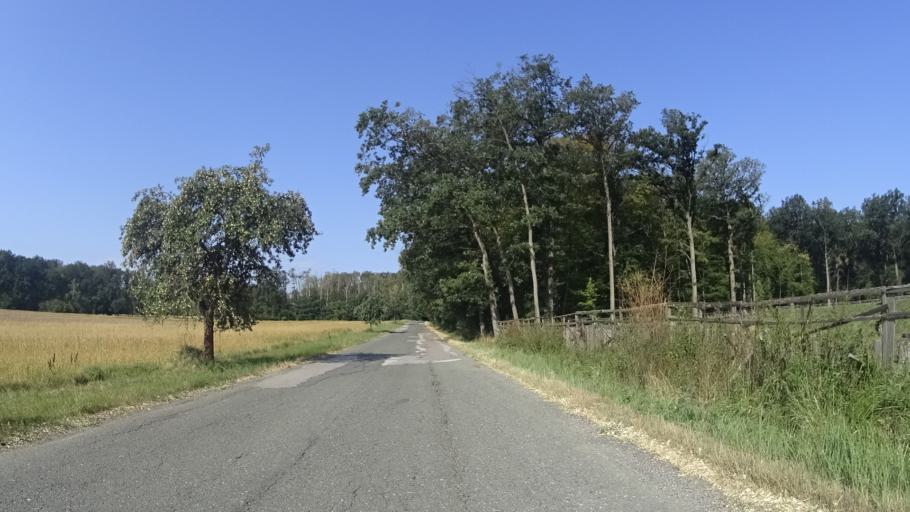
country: CZ
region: Kralovehradecky
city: Novy Bydzov
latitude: 50.2795
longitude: 15.5347
